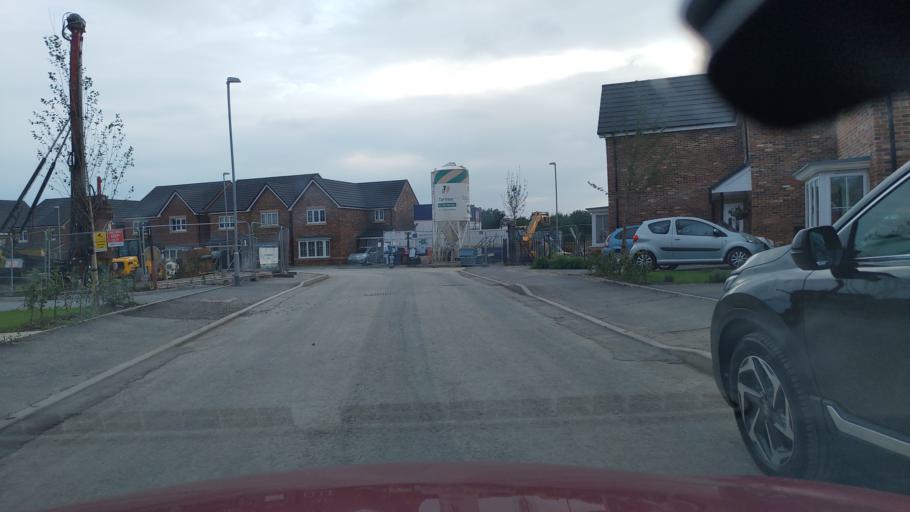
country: GB
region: England
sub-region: Lancashire
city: Coppull
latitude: 53.6282
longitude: -2.6629
